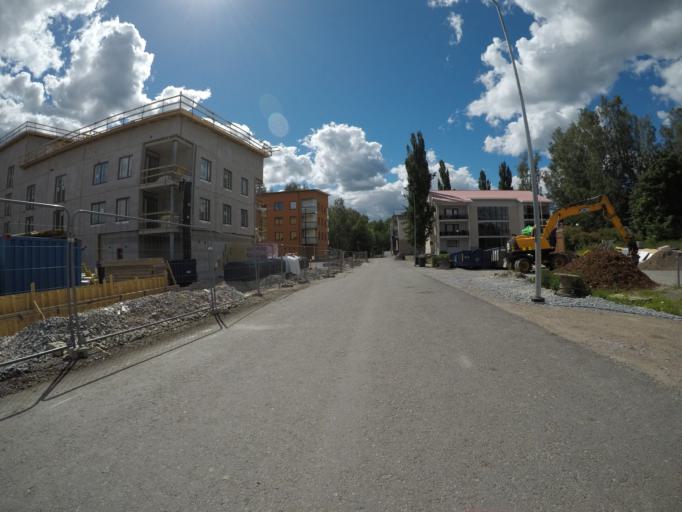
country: FI
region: Haeme
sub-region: Haemeenlinna
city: Haemeenlinna
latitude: 61.0011
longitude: 24.4564
